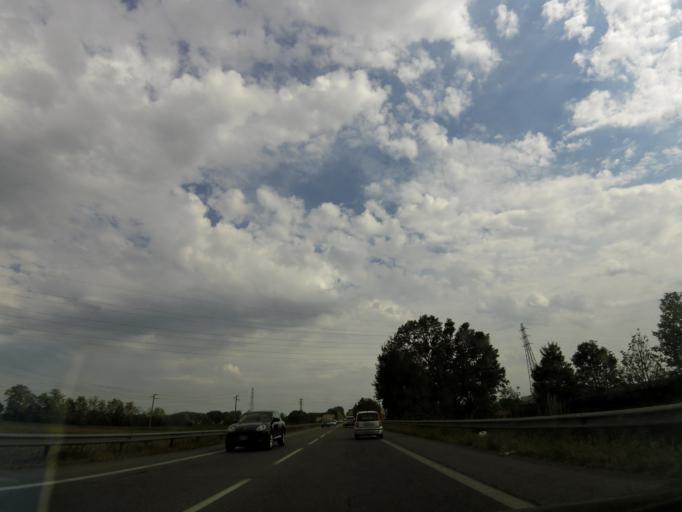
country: IT
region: Lombardy
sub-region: Citta metropolitana di Milano
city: Melegnano
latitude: 45.3714
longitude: 9.3121
